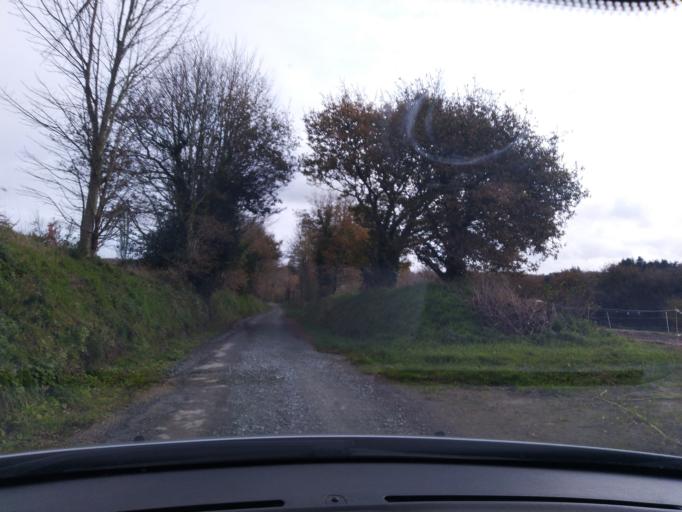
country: FR
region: Brittany
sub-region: Departement du Finistere
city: Guerlesquin
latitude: 48.5173
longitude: -3.5789
